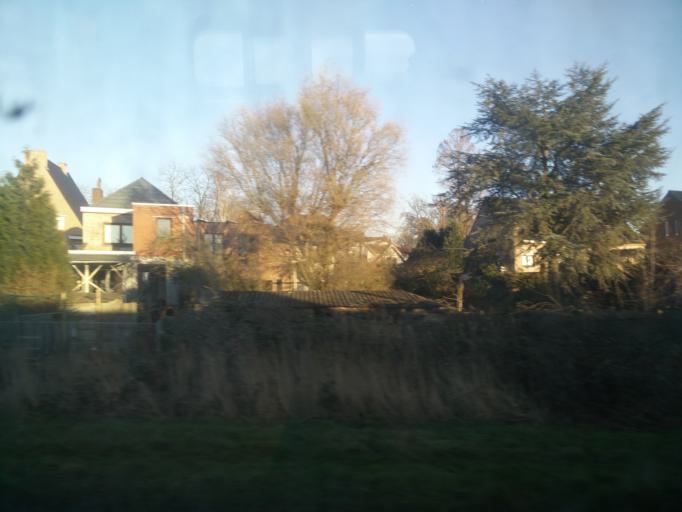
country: BE
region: Flanders
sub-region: Provincie Antwerpen
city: Kapellen
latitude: 51.2785
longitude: 4.4333
